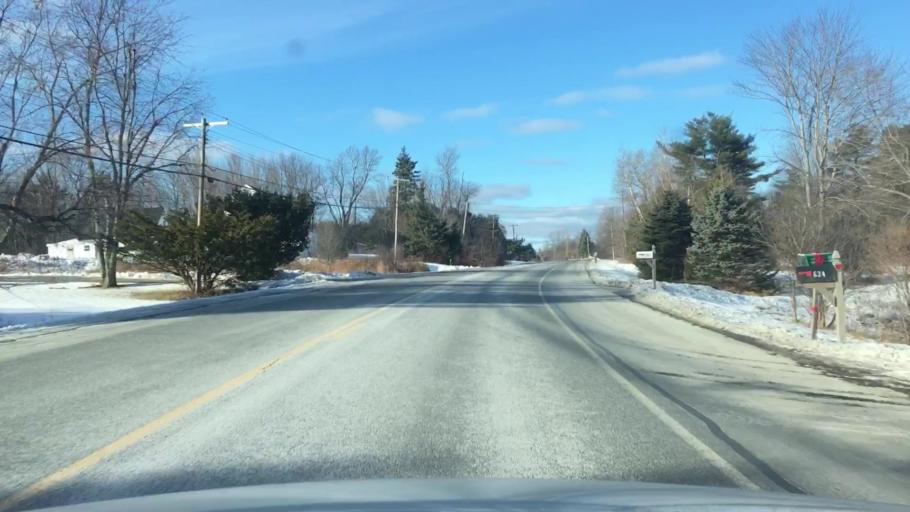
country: US
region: Maine
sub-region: Penobscot County
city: Eddington
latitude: 44.8190
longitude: -68.6474
